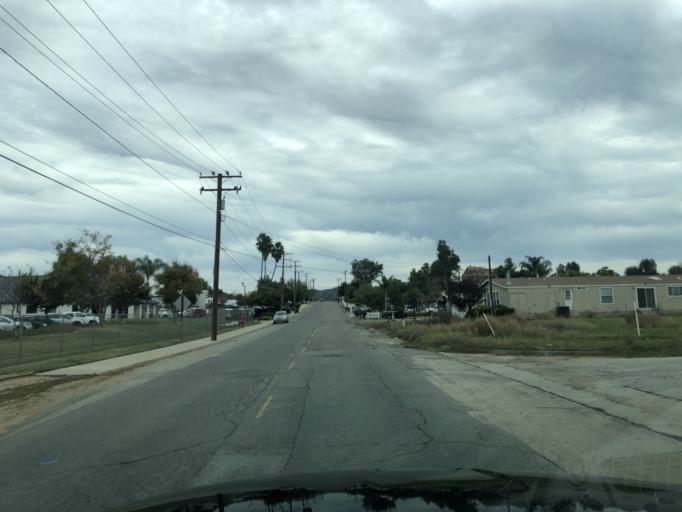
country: US
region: California
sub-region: Riverside County
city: Sedco Hills
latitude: 33.6196
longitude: -117.2887
